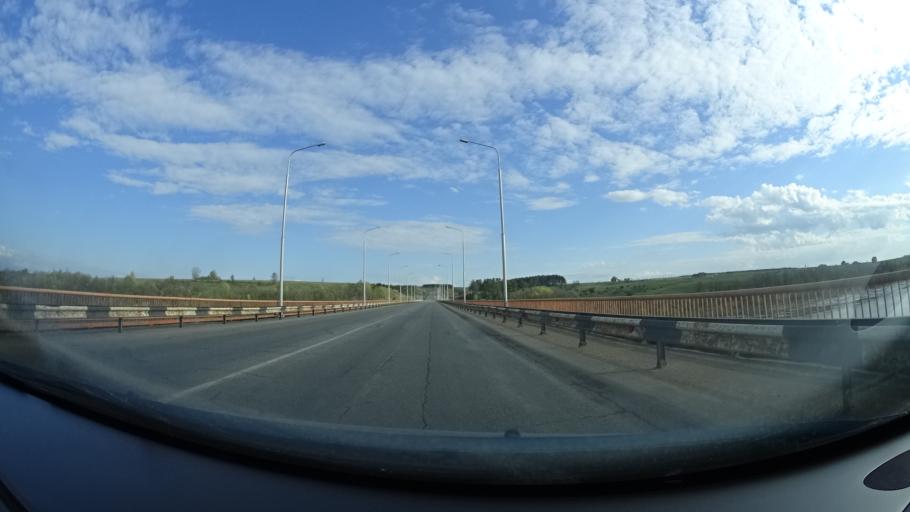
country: RU
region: Bashkortostan
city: Blagoveshchensk
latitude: 55.0689
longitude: 55.8079
